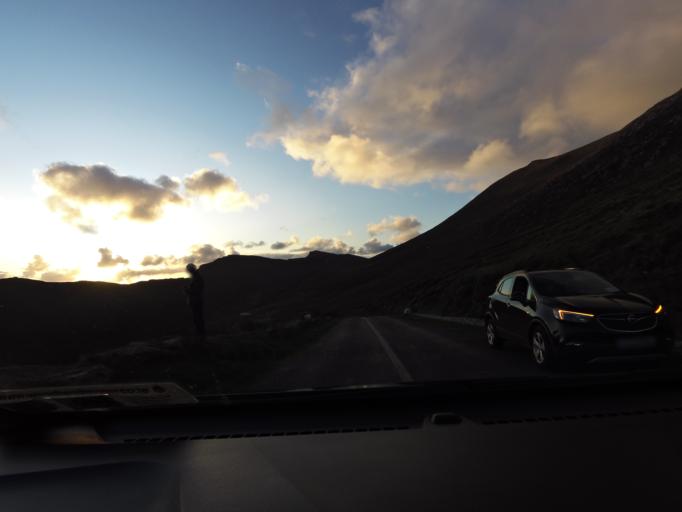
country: IE
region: Connaught
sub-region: Maigh Eo
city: Belmullet
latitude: 53.9703
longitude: -10.1818
